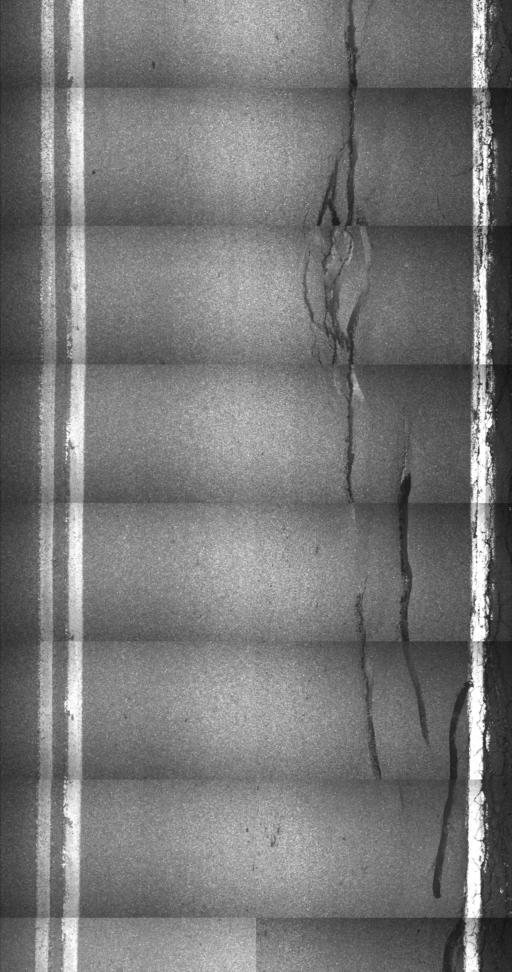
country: US
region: Vermont
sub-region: Rutland County
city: Castleton
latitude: 43.7166
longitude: -73.1854
